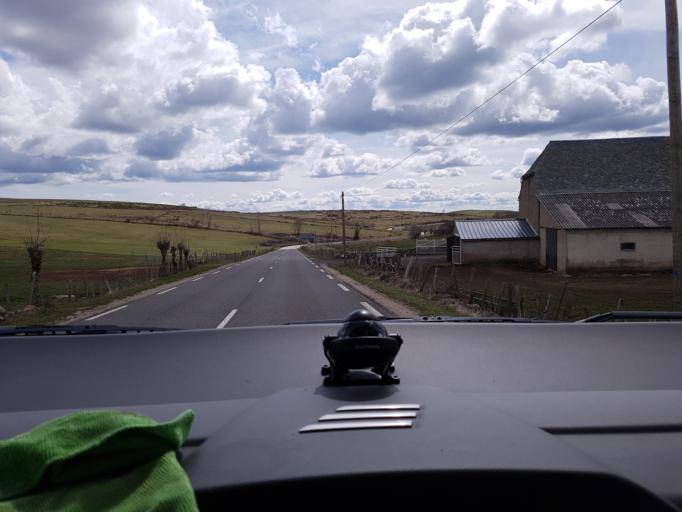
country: FR
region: Midi-Pyrenees
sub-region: Departement de l'Aveyron
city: Laguiole
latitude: 44.7236
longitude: 2.8696
